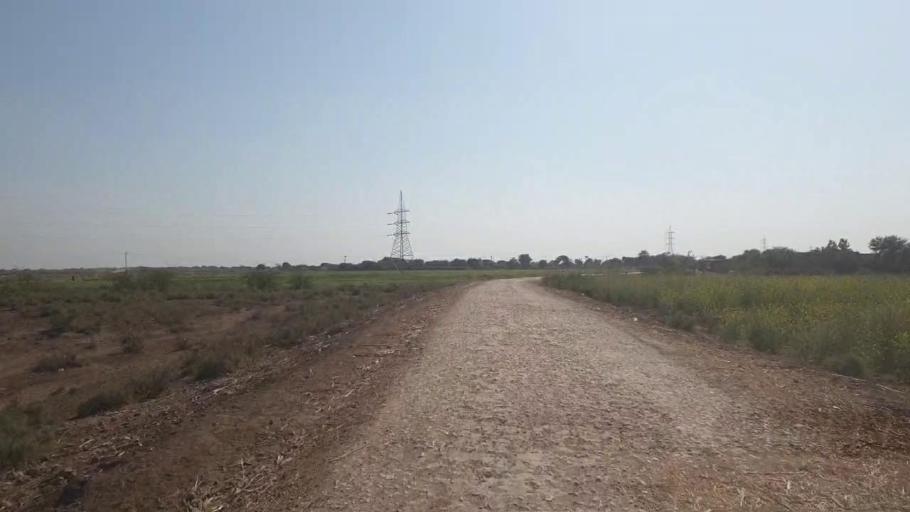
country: PK
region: Sindh
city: Chambar
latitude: 25.2961
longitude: 68.8291
